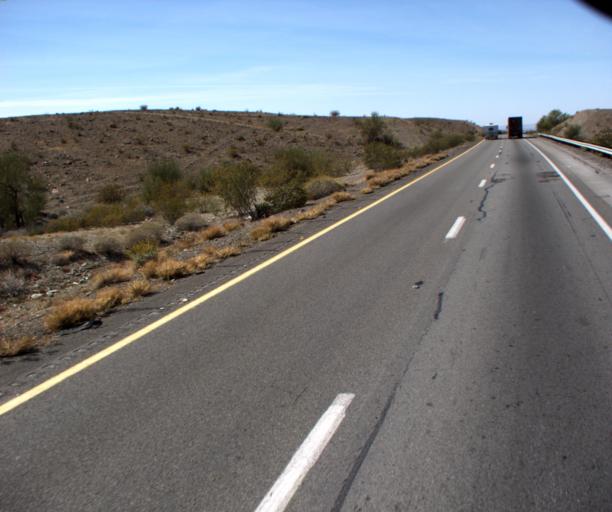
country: US
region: Arizona
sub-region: La Paz County
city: Ehrenberg
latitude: 33.6340
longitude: -114.4009
